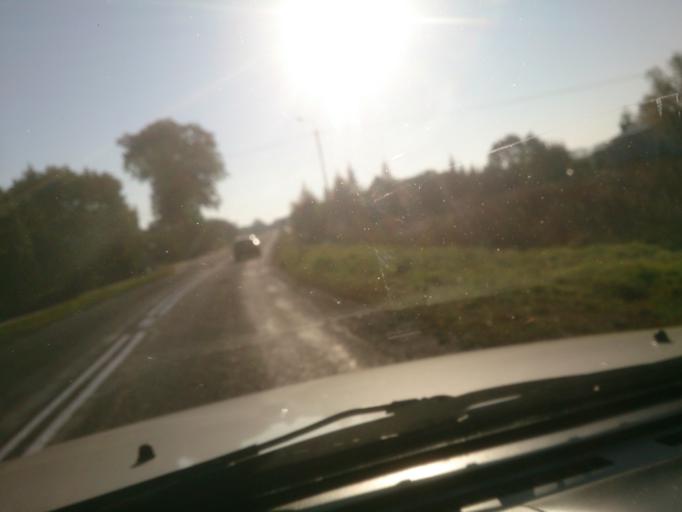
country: PL
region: Kujawsko-Pomorskie
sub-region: Powiat brodnicki
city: Brodnica
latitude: 53.2404
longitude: 19.4989
